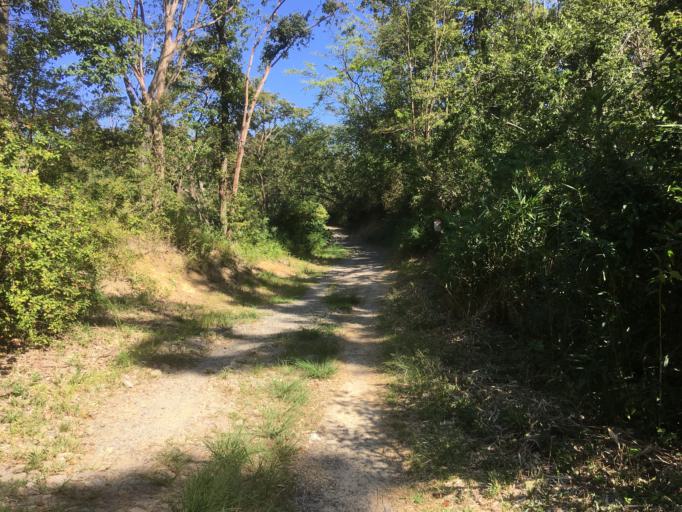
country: JP
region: Nara
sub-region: Ikoma-shi
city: Ikoma
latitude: 34.7247
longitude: 135.6702
